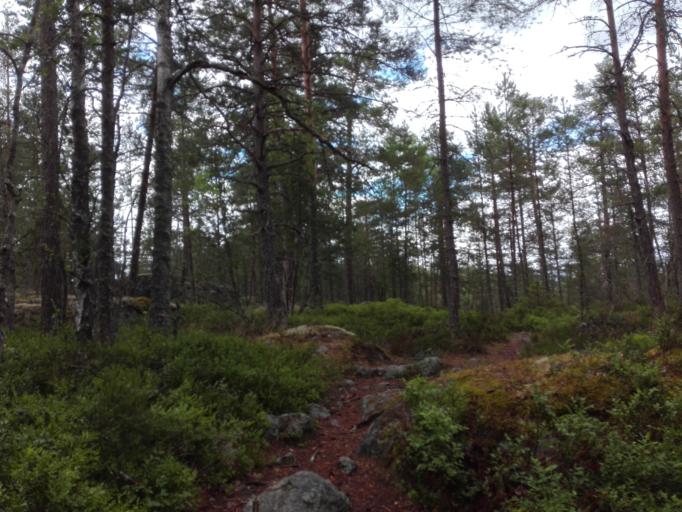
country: SE
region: Stockholm
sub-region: Nacka Kommun
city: Fisksatra
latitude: 59.2787
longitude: 18.2601
